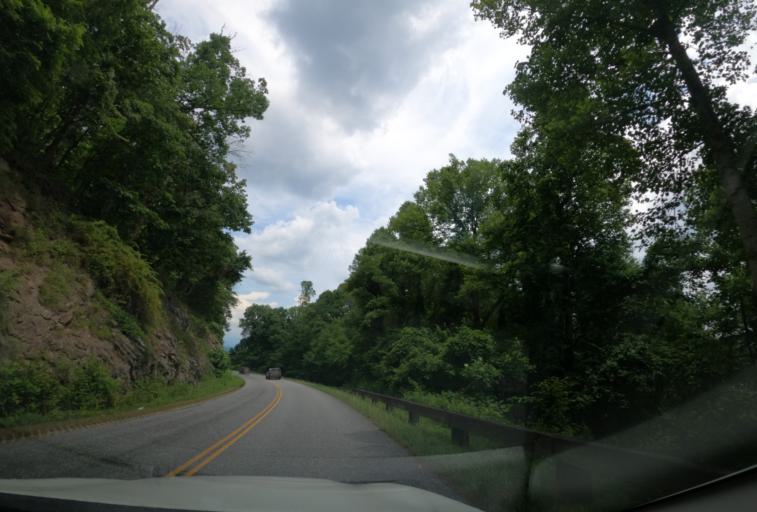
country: US
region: North Carolina
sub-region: Buncombe County
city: Avery Creek
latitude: 35.4744
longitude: -82.6027
